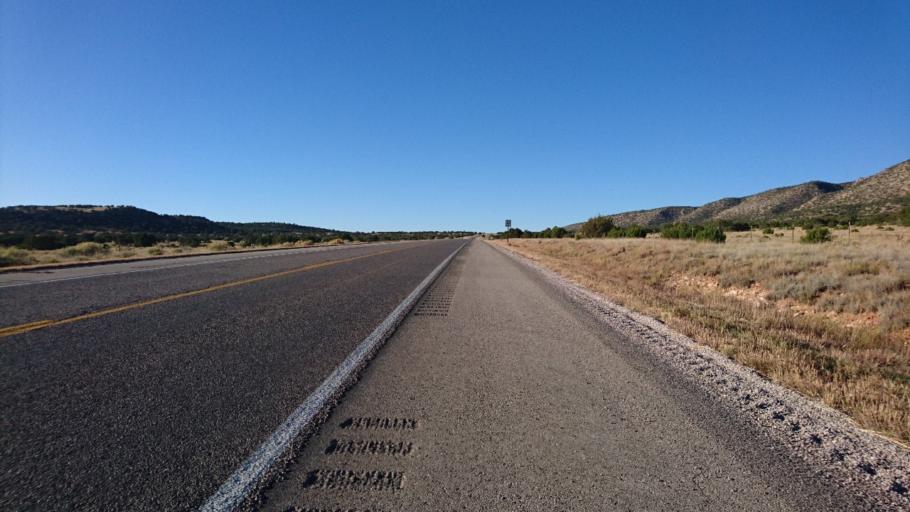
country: US
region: New Mexico
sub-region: Cibola County
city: Grants
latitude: 35.0130
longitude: -107.8889
